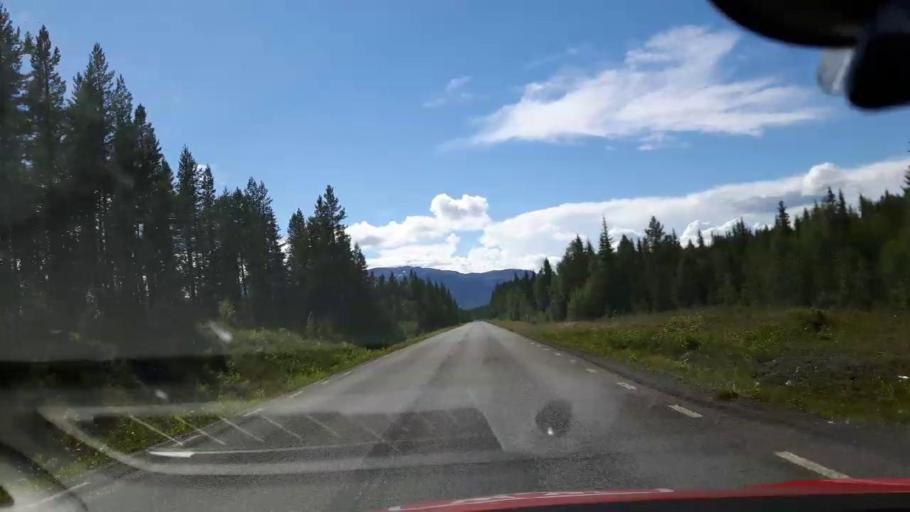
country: SE
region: Jaemtland
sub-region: Are Kommun
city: Are
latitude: 63.2232
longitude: 13.1185
